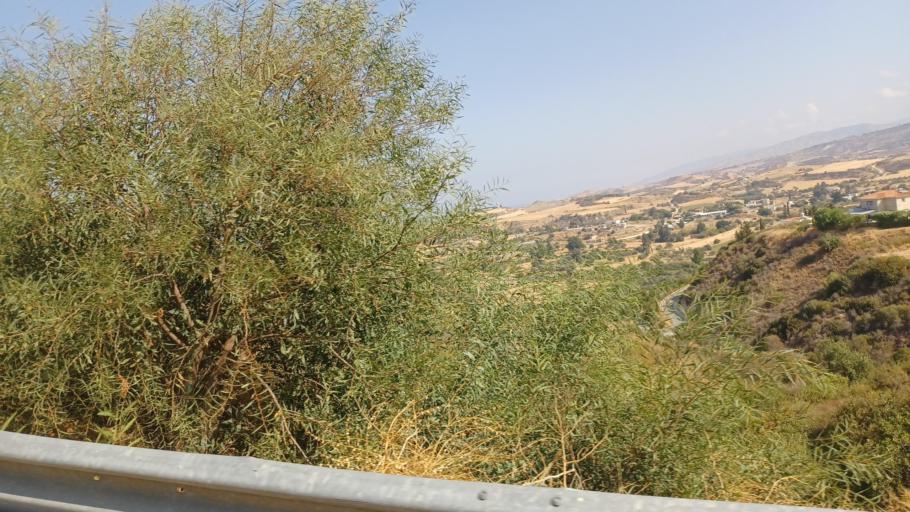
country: CY
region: Pafos
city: Polis
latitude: 34.9960
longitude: 32.4332
